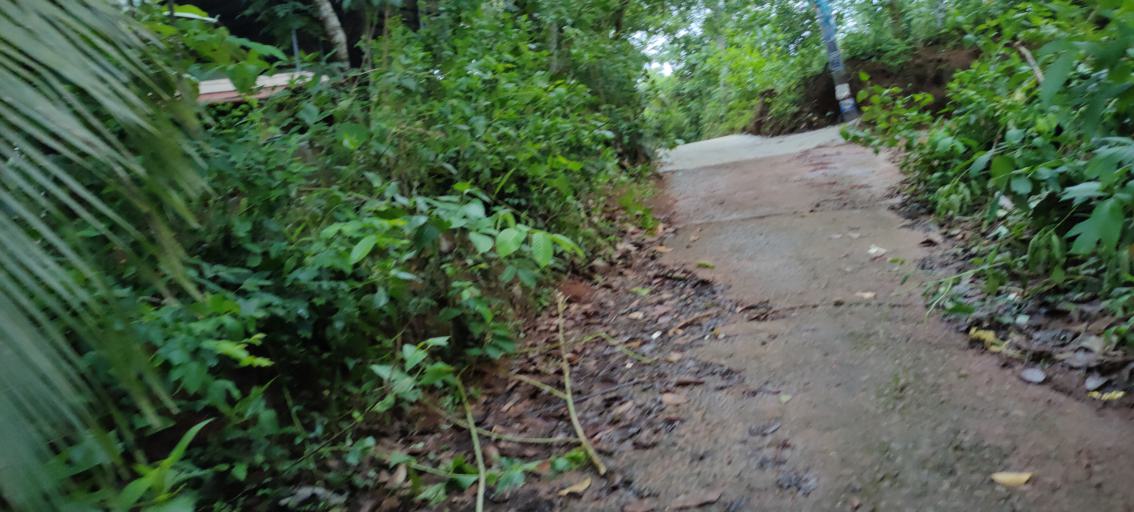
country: IN
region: Kerala
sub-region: Malappuram
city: Ponnani
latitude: 10.7669
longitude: 76.0331
